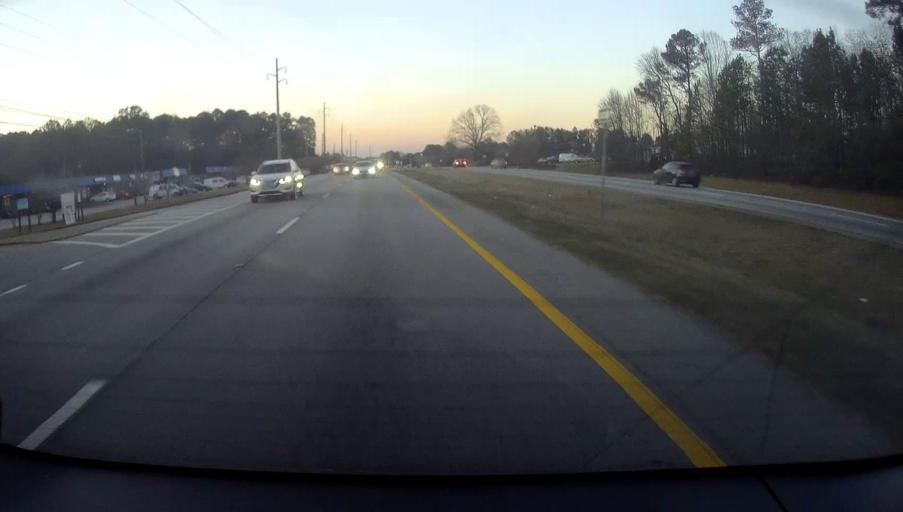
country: US
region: Georgia
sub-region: Fayette County
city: Fayetteville
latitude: 33.5049
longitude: -84.4281
